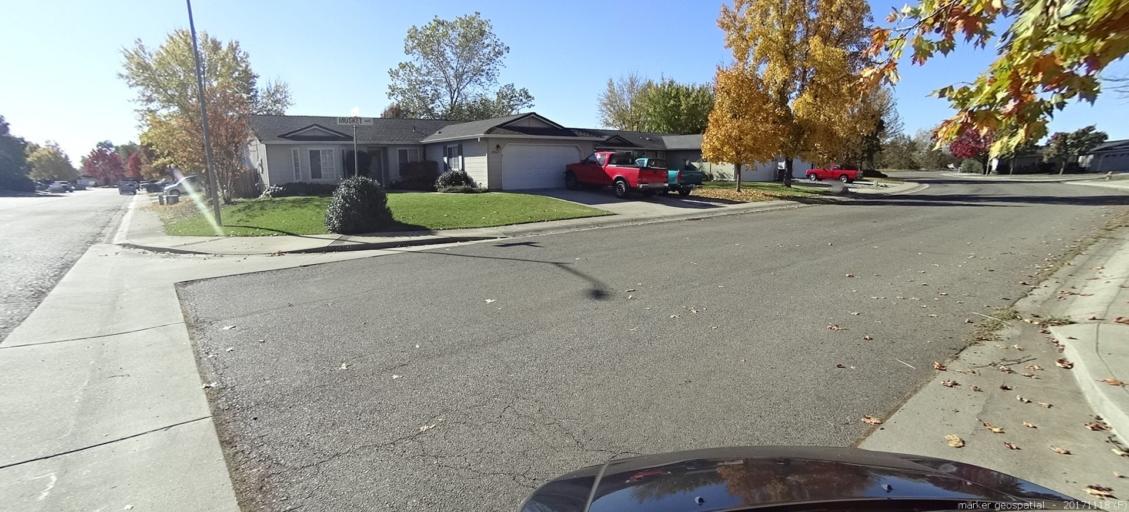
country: US
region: California
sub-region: Shasta County
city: Cottonwood
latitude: 40.3917
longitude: -122.2784
